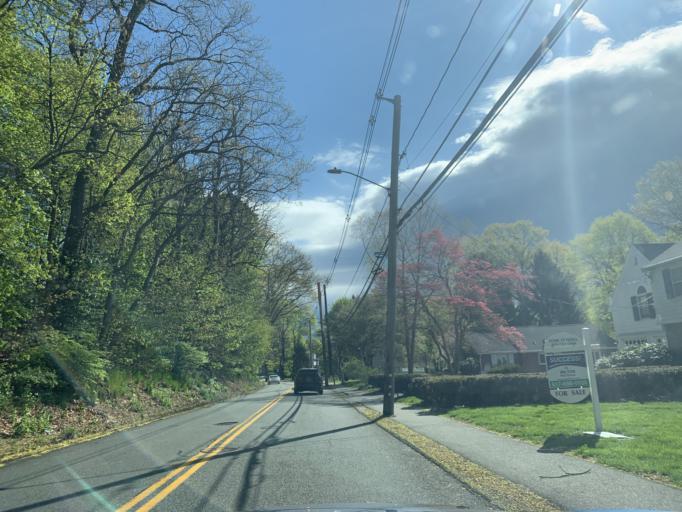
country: US
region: Massachusetts
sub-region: Norfolk County
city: Milton
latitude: 42.2594
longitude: -71.0535
